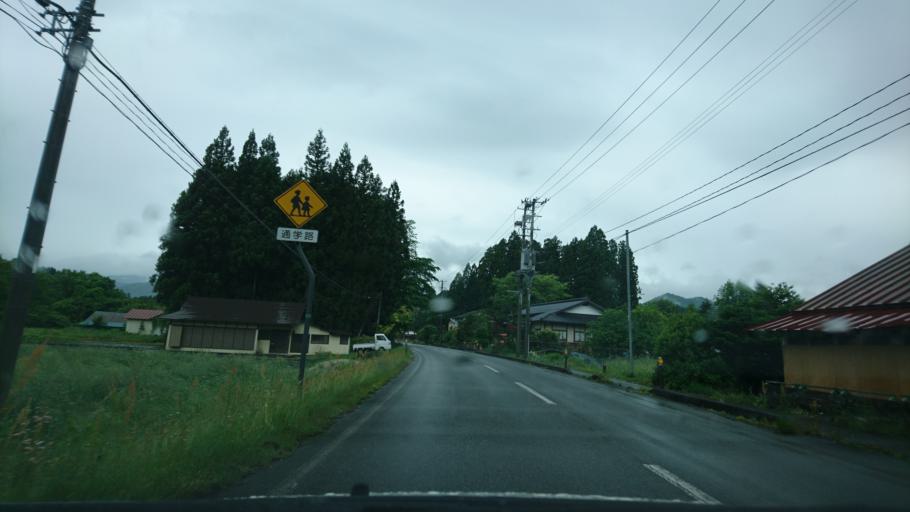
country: JP
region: Iwate
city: Ichinoseki
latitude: 38.9732
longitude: 140.9534
